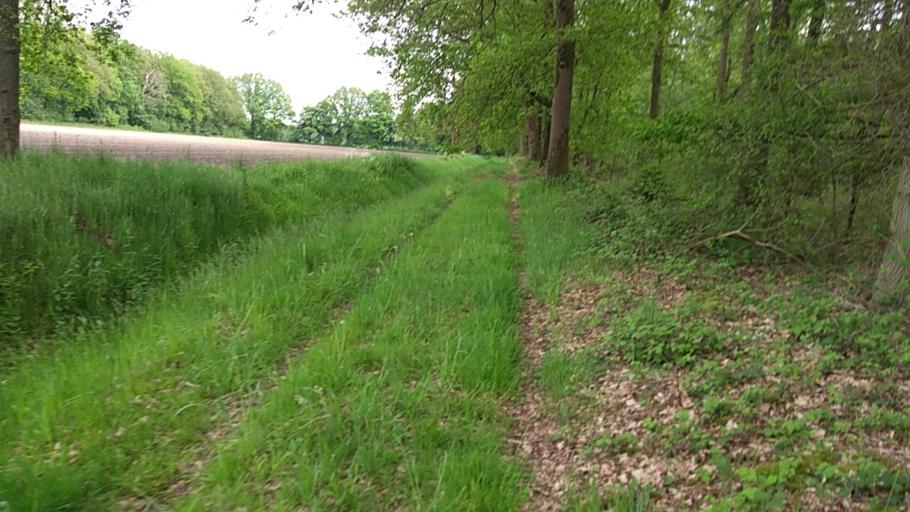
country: NL
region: Limburg
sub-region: Gemeente Nederweert
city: Nederweert
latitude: 51.2912
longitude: 5.8189
